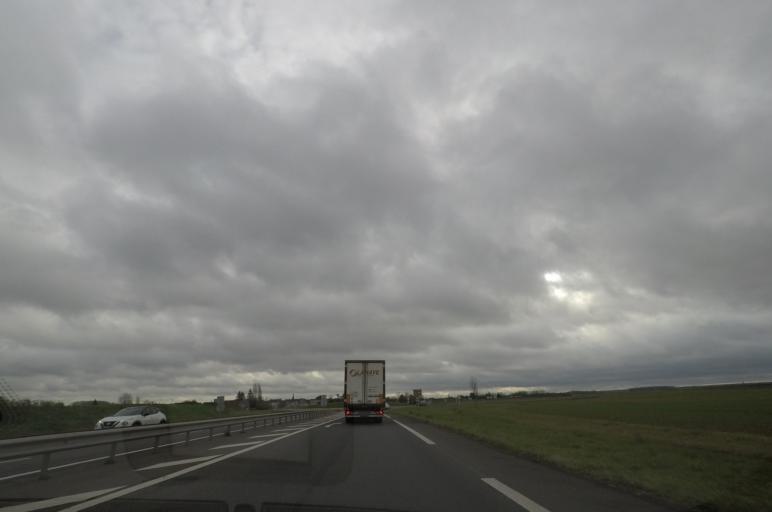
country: FR
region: Centre
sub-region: Departement du Loir-et-Cher
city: Saint-Sulpice-de-Pommeray
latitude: 47.6746
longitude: 1.2294
